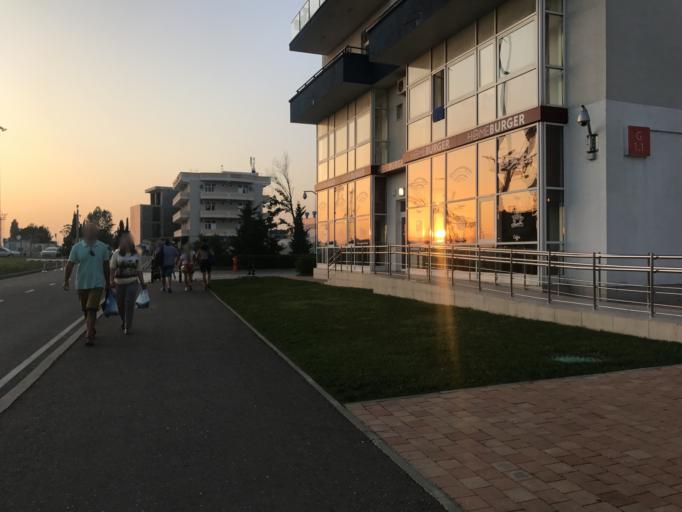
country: RU
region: Krasnodarskiy
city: Adler
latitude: 43.4129
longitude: 39.9324
